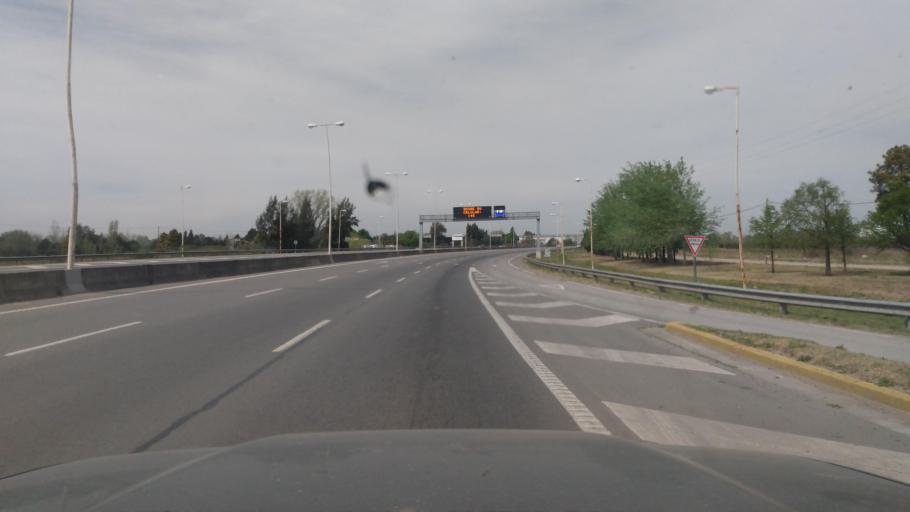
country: AR
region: Buenos Aires
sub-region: Partido de Pilar
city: Pilar
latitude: -34.4102
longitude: -59.0057
